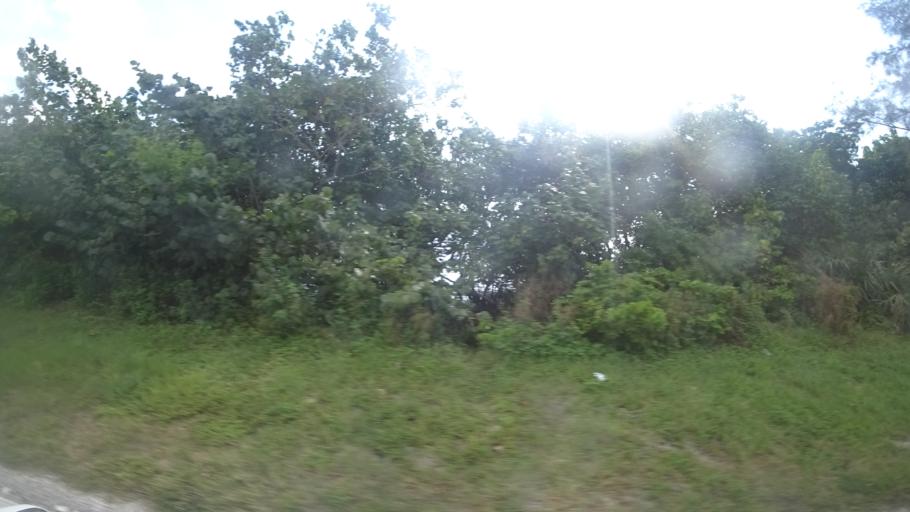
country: US
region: Florida
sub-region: Manatee County
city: West Bradenton
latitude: 27.5222
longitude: -82.6069
